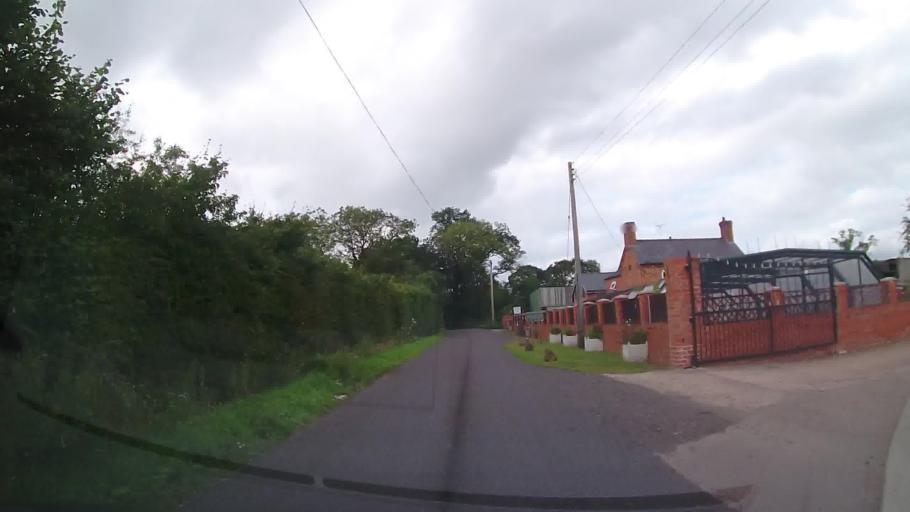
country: GB
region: England
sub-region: Shropshire
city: Whitchurch
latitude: 52.9246
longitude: -2.7304
